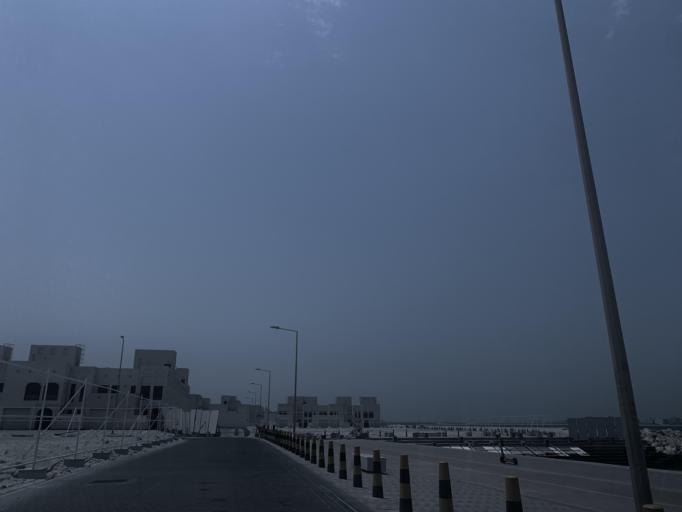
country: BH
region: Muharraq
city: Al Hadd
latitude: 26.2404
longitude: 50.6736
